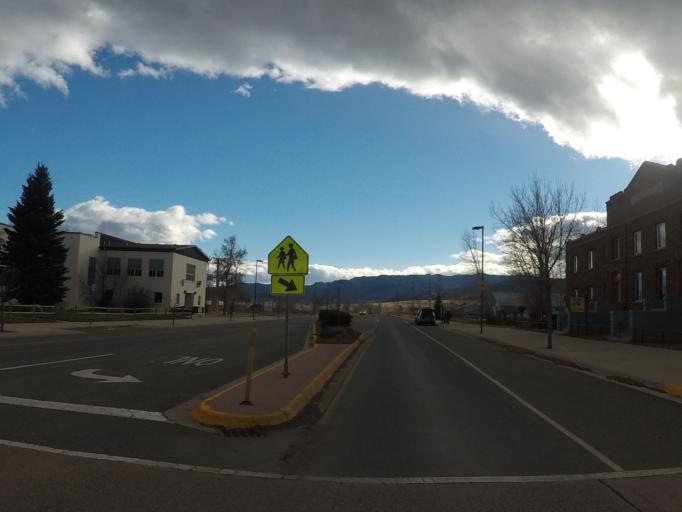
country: US
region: Montana
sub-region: Jefferson County
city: Boulder
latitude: 46.2342
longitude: -112.1202
